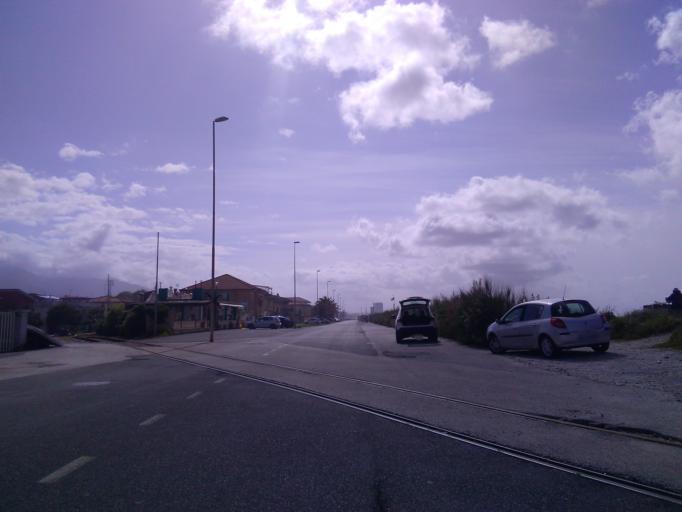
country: IT
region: Tuscany
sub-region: Provincia di Massa-Carrara
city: Marina di Carrara
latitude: 44.0312
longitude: 10.0561
